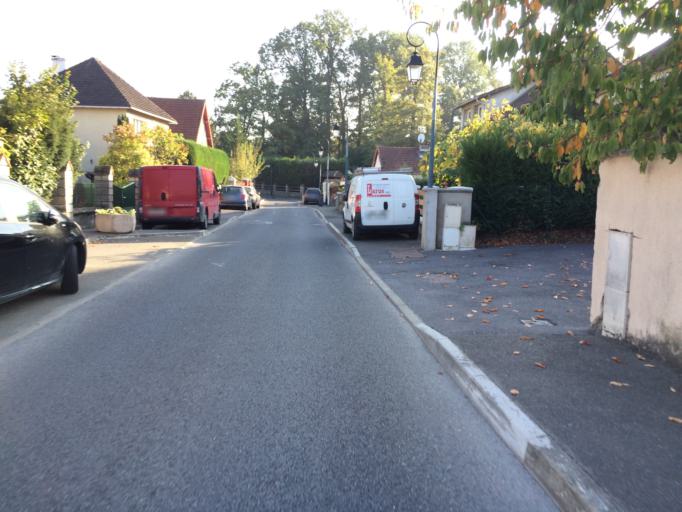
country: FR
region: Ile-de-France
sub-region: Departement de l'Essonne
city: Villejust
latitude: 48.6921
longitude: 2.2462
